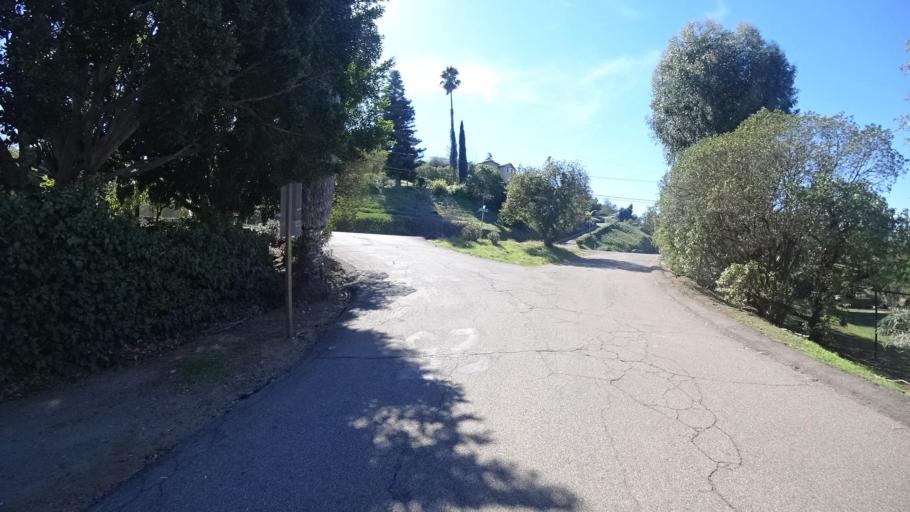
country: US
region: California
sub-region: San Diego County
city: Casa de Oro-Mount Helix
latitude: 32.7617
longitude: -116.9676
